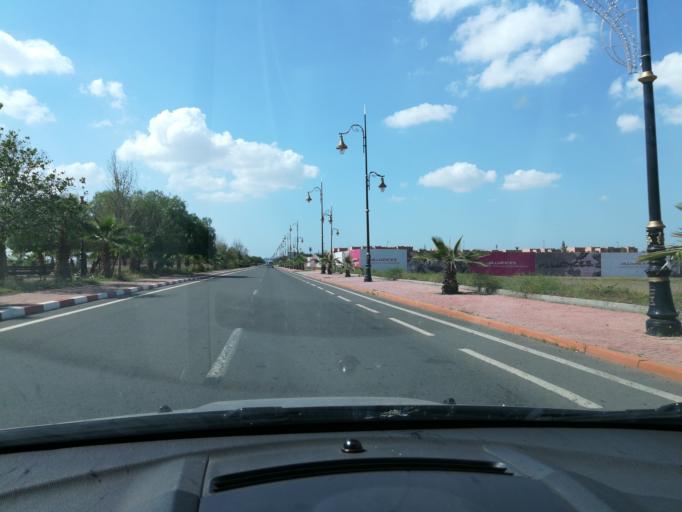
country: MA
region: Marrakech-Tensift-Al Haouz
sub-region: Marrakech
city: Marrakesh
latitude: 31.5843
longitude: -7.9860
